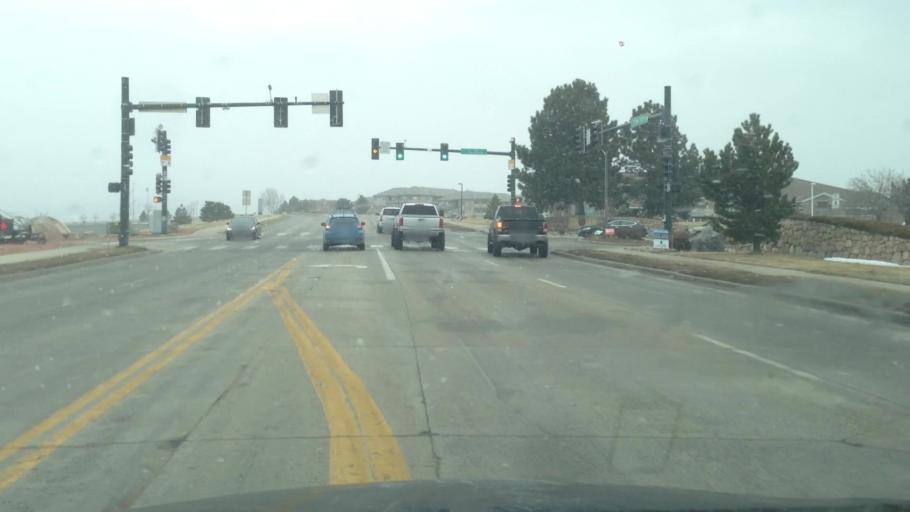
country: US
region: Colorado
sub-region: Douglas County
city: Castle Rock
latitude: 39.3630
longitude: -104.8577
